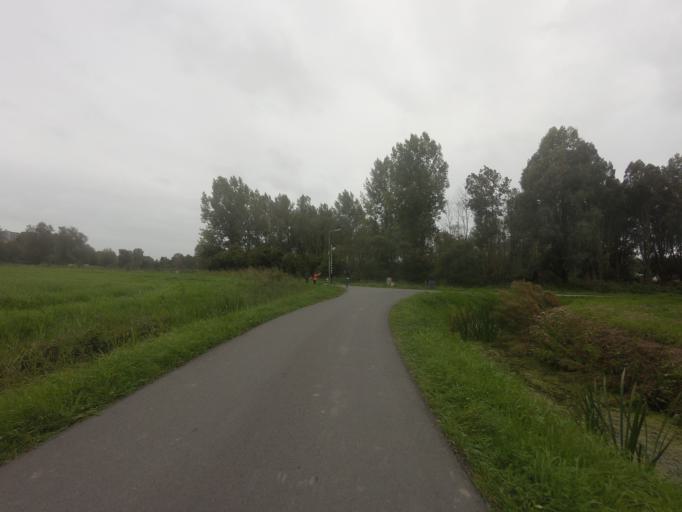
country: NL
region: Friesland
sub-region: Gemeente Leeuwarden
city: Bilgaard
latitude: 53.2208
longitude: 5.7897
